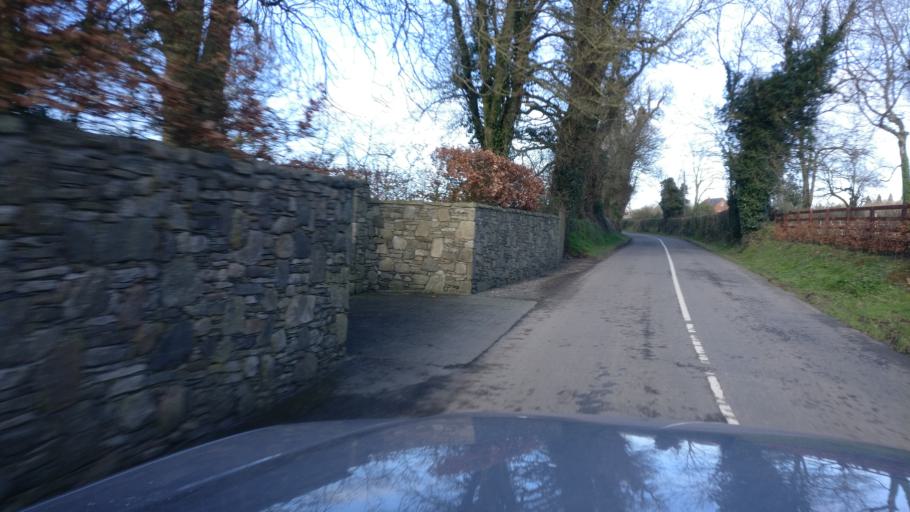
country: IE
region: Leinster
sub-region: Kilkenny
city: Castlecomer
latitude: 52.8859
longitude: -7.1615
